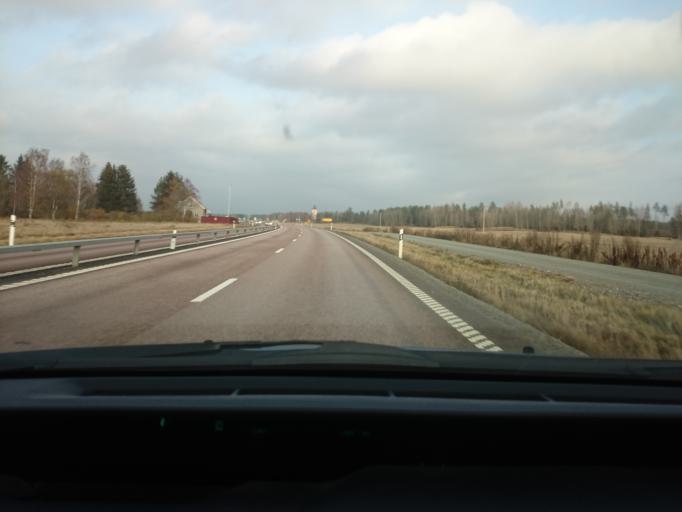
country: SE
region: Vaestmanland
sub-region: Sala Kommun
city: Sala
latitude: 59.8608
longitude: 16.5399
